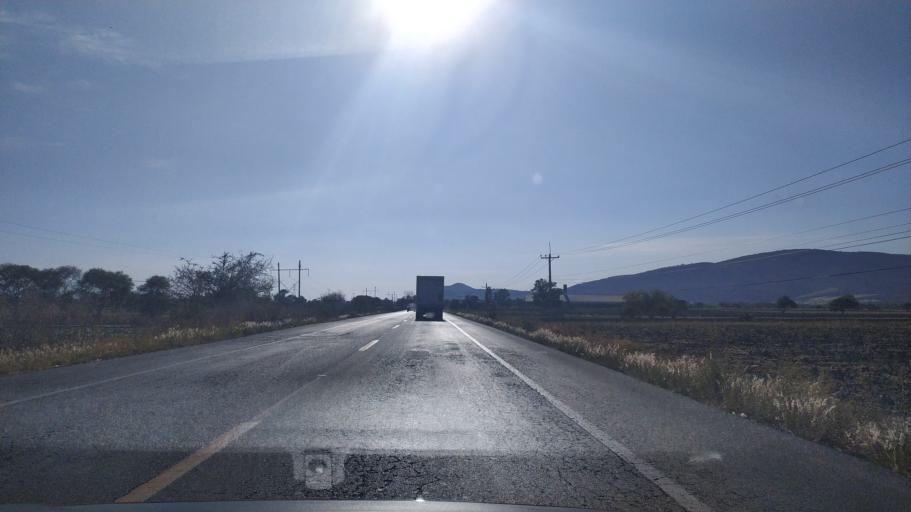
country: MX
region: Jalisco
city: Jamay
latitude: 20.2936
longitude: -102.6469
